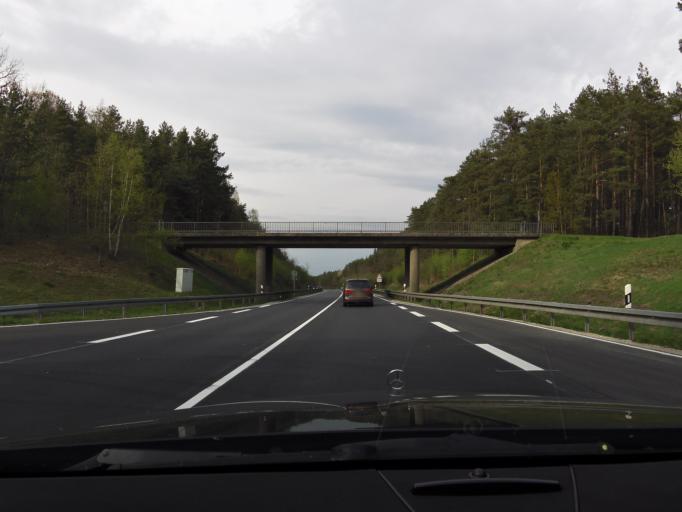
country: DE
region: Bavaria
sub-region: Regierungsbezirk Mittelfranken
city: Hochstadt an der Aisch
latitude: 49.7310
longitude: 10.8252
